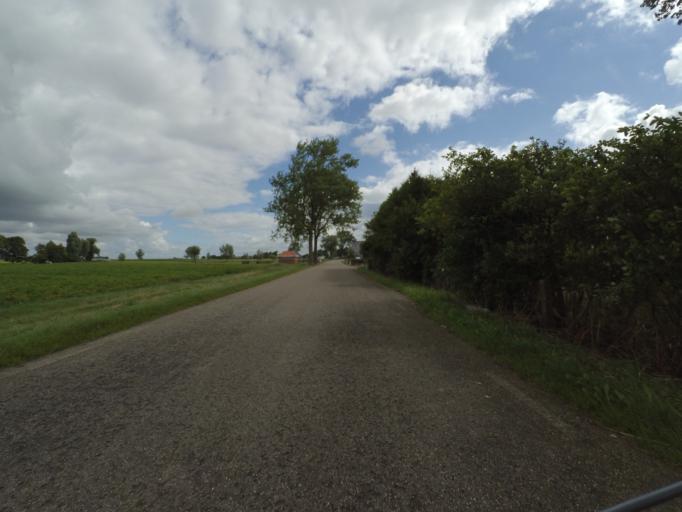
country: NL
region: Groningen
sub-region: Gemeente Zuidhorn
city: Grijpskerk
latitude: 53.2985
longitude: 6.2429
